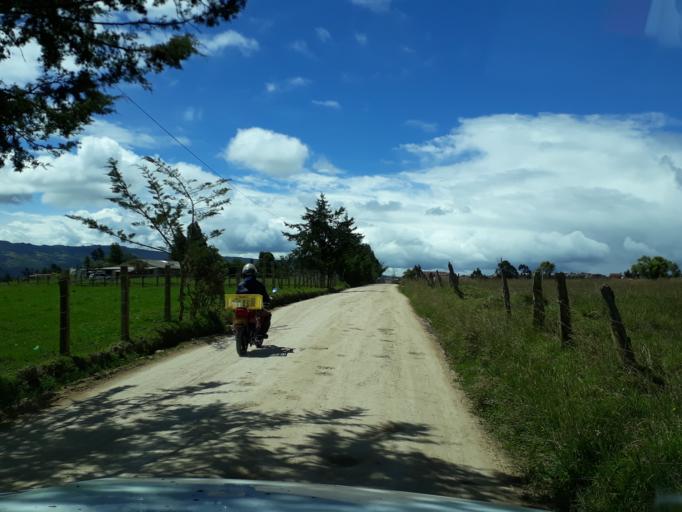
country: CO
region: Cundinamarca
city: Guasca
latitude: 4.8558
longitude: -73.8793
